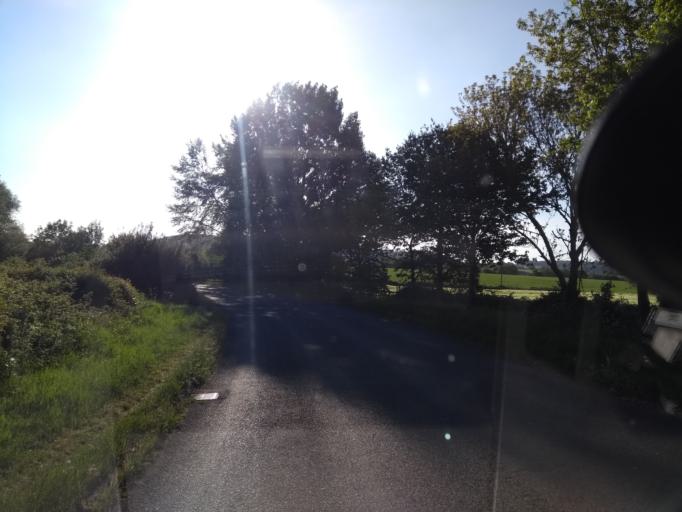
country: GB
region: England
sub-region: Somerset
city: Taunton
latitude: 50.9992
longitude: -3.0759
